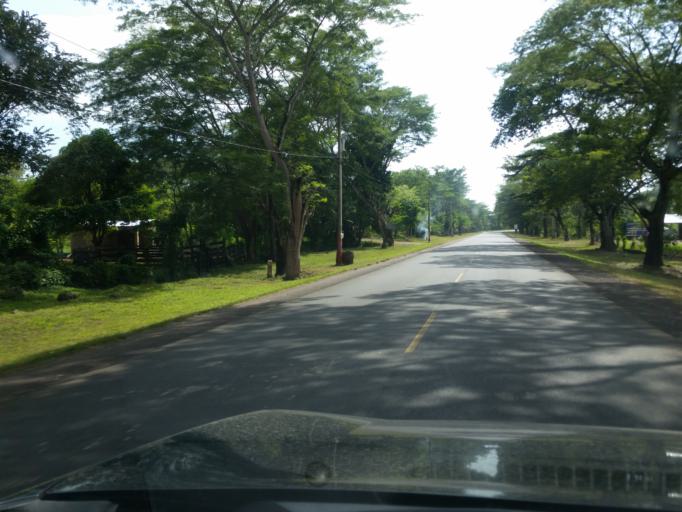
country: NI
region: Rio San Juan
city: San Miguelito
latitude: 11.5443
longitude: -84.8251
